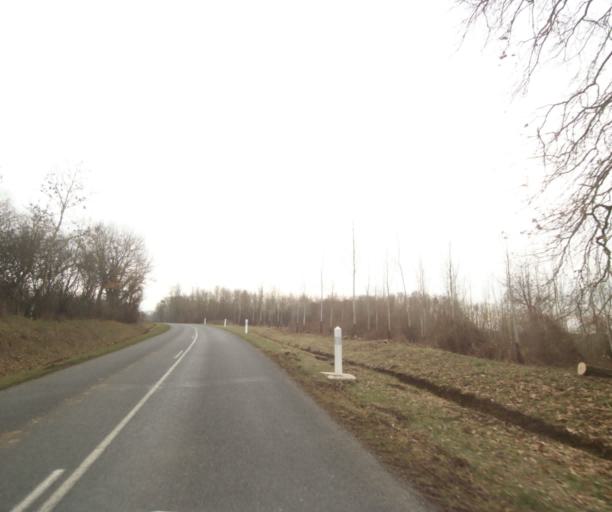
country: FR
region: Champagne-Ardenne
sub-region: Departement de la Marne
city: Pargny-sur-Saulx
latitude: 48.7402
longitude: 4.8529
